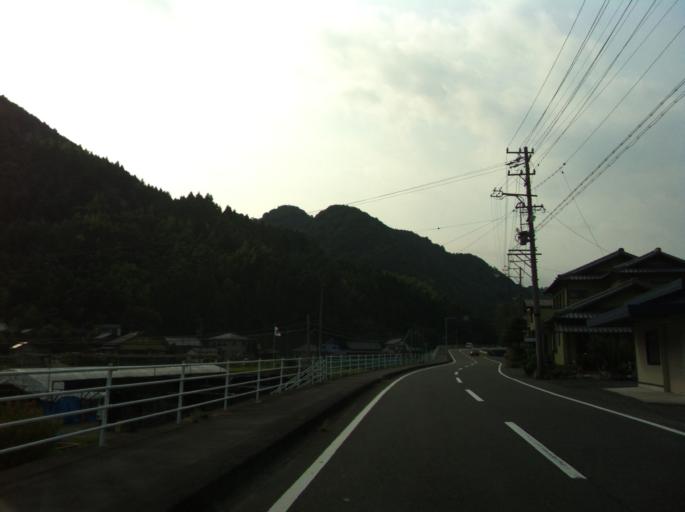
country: JP
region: Shizuoka
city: Fujieda
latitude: 34.9338
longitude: 138.2637
